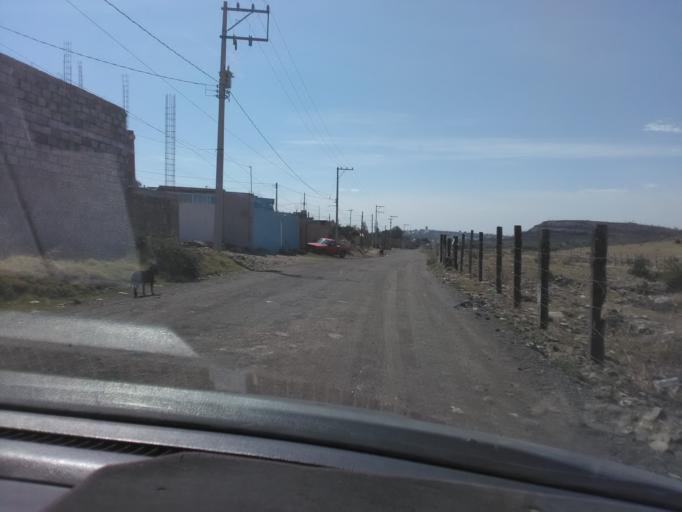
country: MX
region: Durango
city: Victoria de Durango
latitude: 24.0328
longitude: -104.7141
